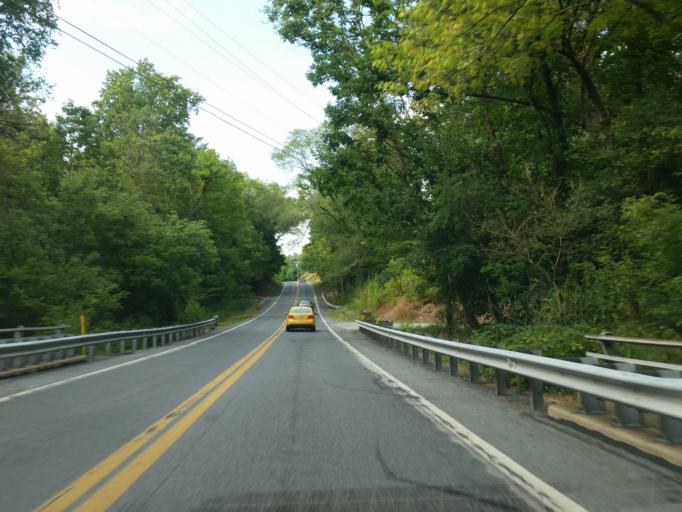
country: US
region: Pennsylvania
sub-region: Lebanon County
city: Annville
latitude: 40.3561
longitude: -76.5275
